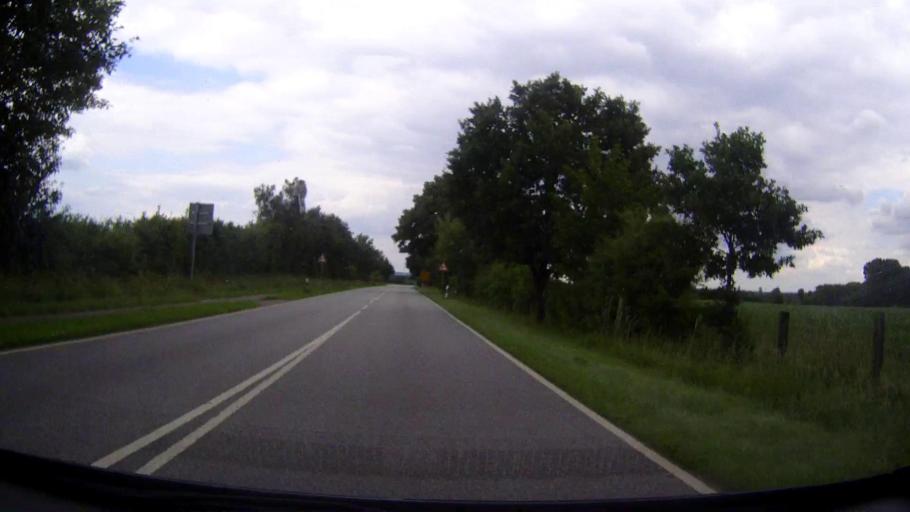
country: DE
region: Schleswig-Holstein
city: Reher
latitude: 54.0729
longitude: 9.5784
